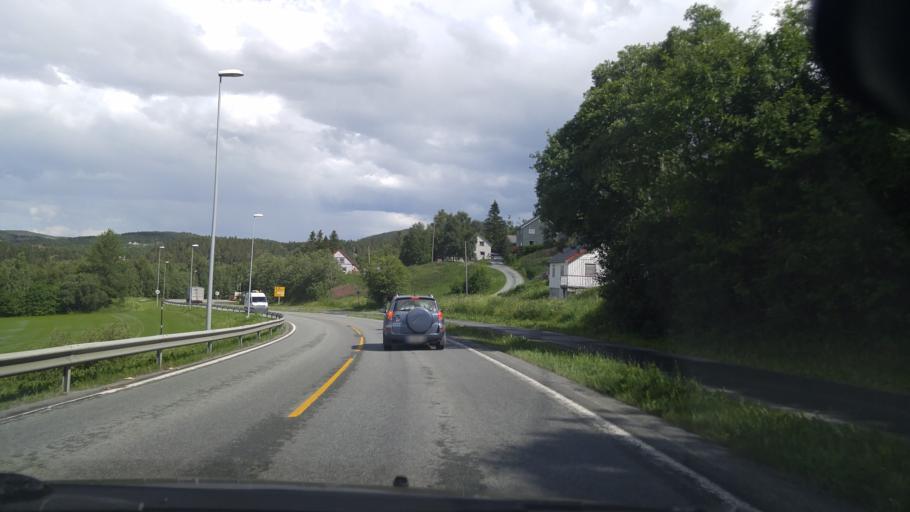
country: NO
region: Nord-Trondelag
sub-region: Levanger
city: Skogn
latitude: 63.6165
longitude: 11.0631
